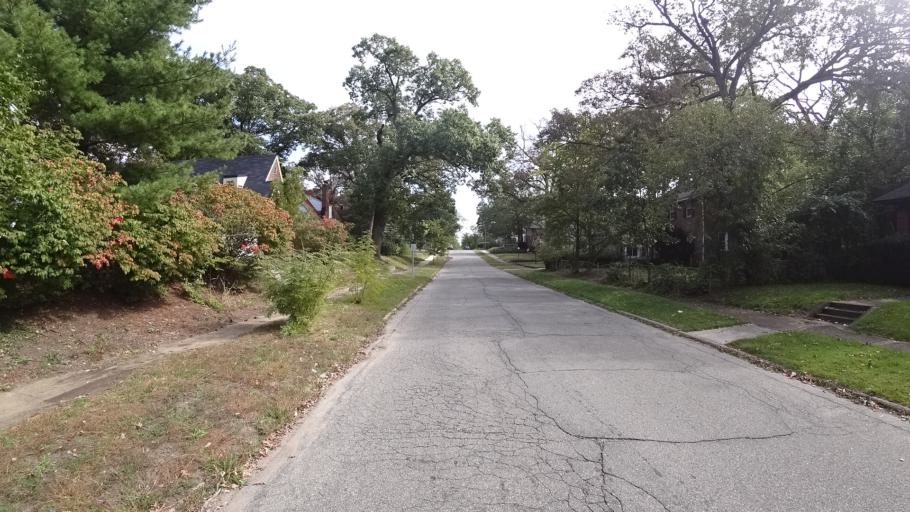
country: US
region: Indiana
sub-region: LaPorte County
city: Michigan City
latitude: 41.7143
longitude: -86.8817
